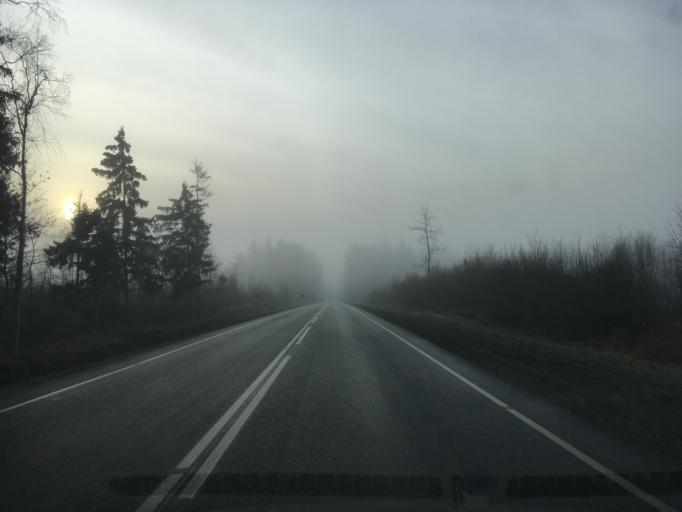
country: EE
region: Harju
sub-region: Anija vald
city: Kehra
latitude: 59.3677
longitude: 25.3203
